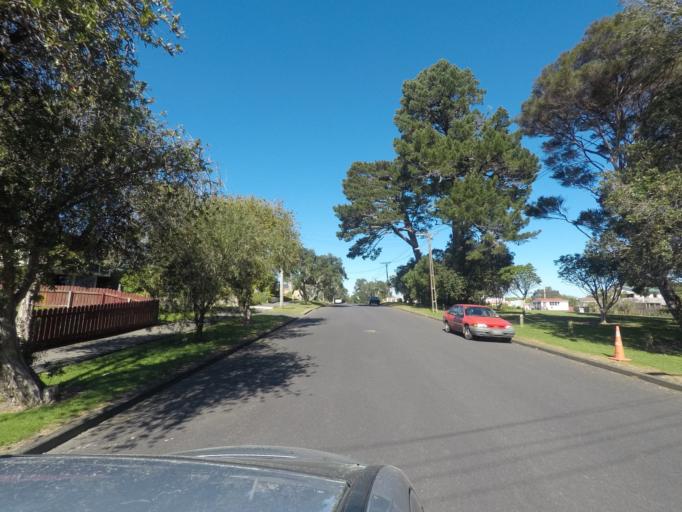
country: NZ
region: Auckland
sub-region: Auckland
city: Waitakere
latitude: -36.9265
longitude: 174.6945
